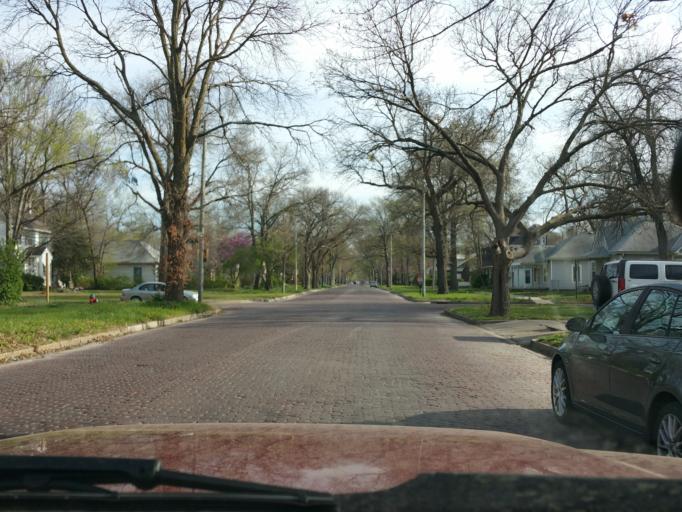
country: US
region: Kansas
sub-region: Riley County
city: Manhattan
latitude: 39.1851
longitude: -96.5667
